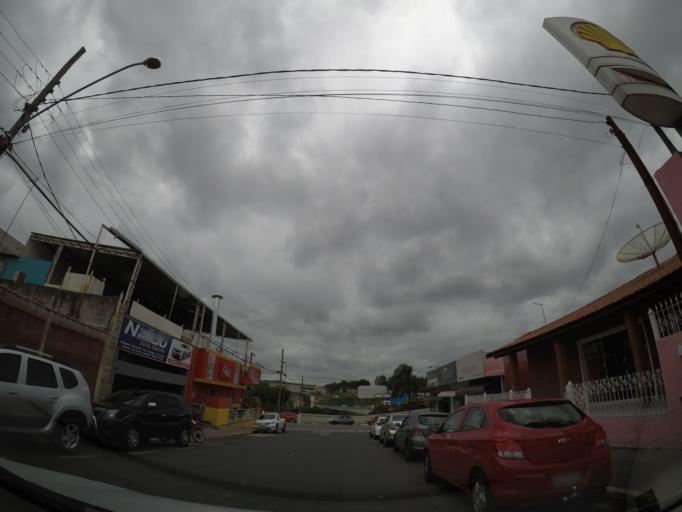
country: BR
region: Sao Paulo
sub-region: Louveira
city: Louveira
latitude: -23.0855
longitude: -46.9771
